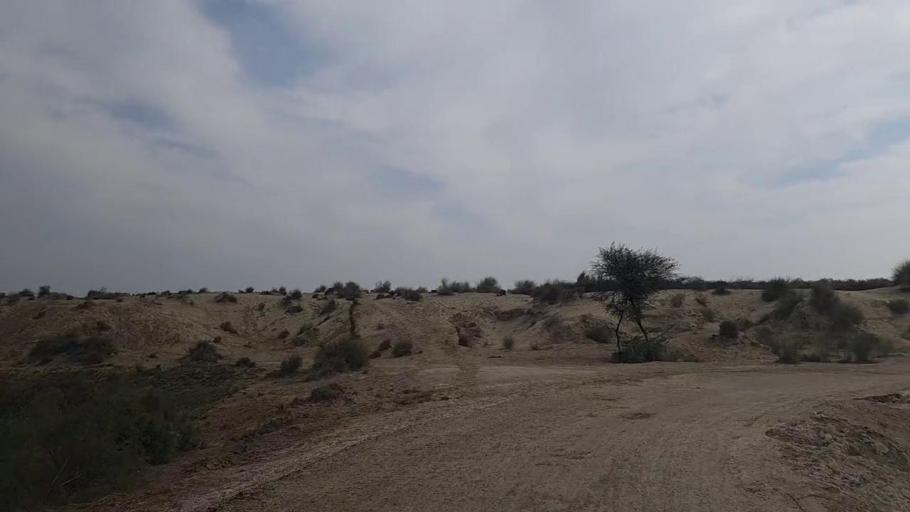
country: PK
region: Sindh
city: Daur
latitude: 26.4334
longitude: 68.4720
